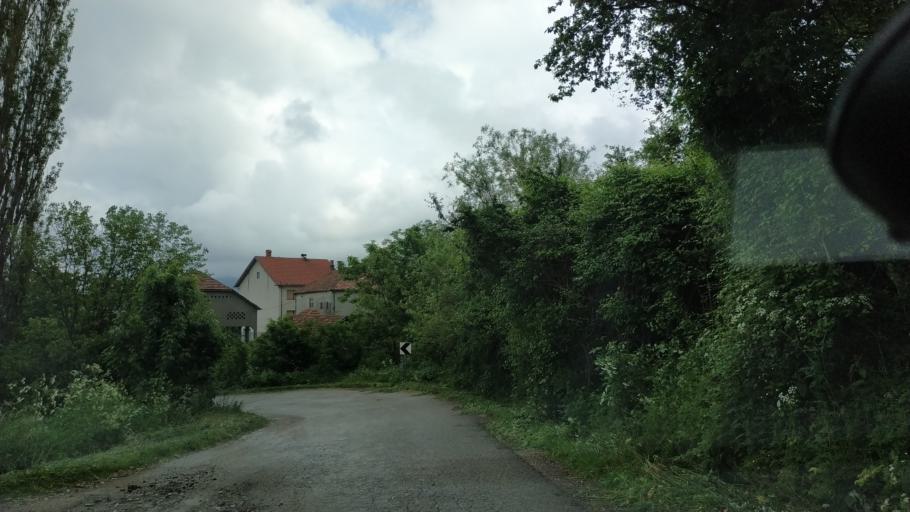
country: RS
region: Central Serbia
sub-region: Toplicki Okrug
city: Prokuplje
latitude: 43.3967
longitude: 21.5550
